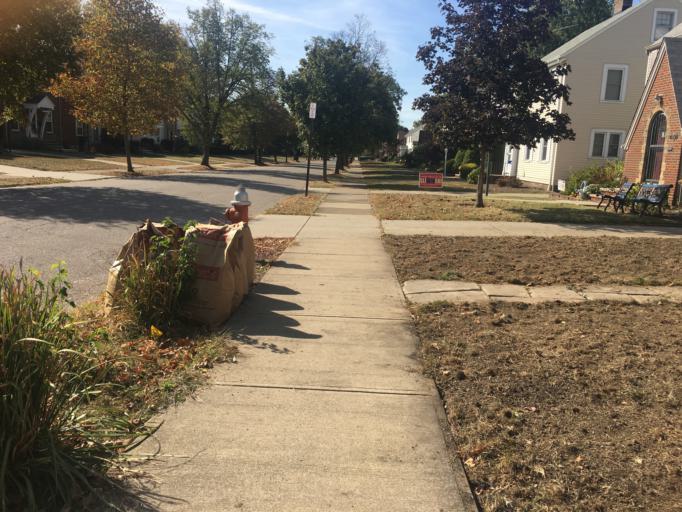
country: US
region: Ohio
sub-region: Cuyahoga County
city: Lakewood
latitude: 41.4607
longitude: -81.8110
